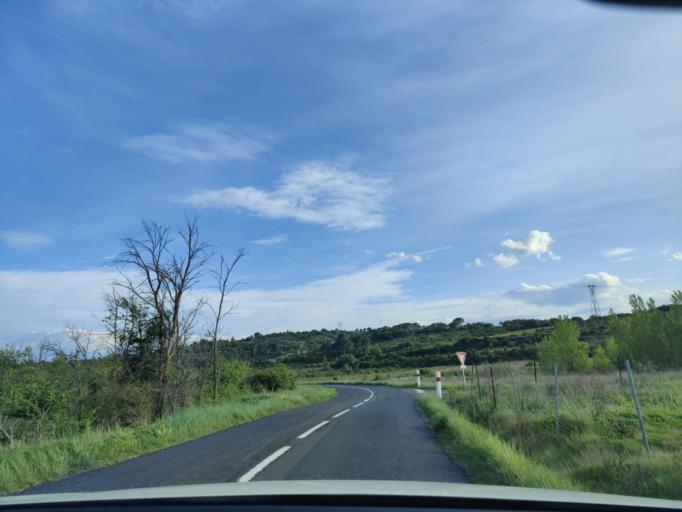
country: FR
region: Languedoc-Roussillon
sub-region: Departement des Pyrenees-Orientales
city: Estagel
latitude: 42.7957
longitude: 2.6981
